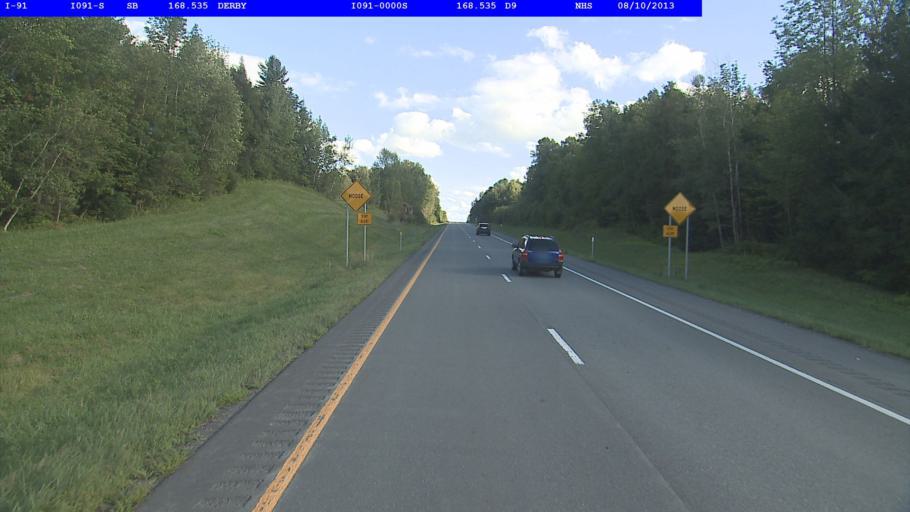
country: US
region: Vermont
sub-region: Orleans County
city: Newport
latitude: 44.9015
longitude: -72.1771
